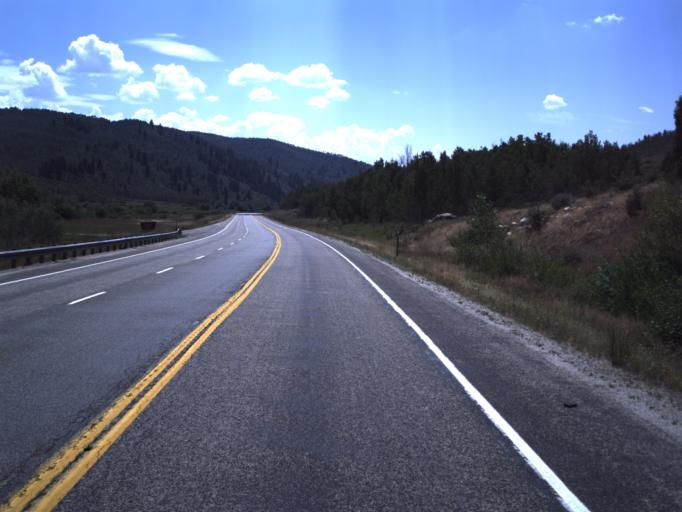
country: US
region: Utah
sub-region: Cache County
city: Richmond
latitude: 41.8772
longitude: -111.5647
